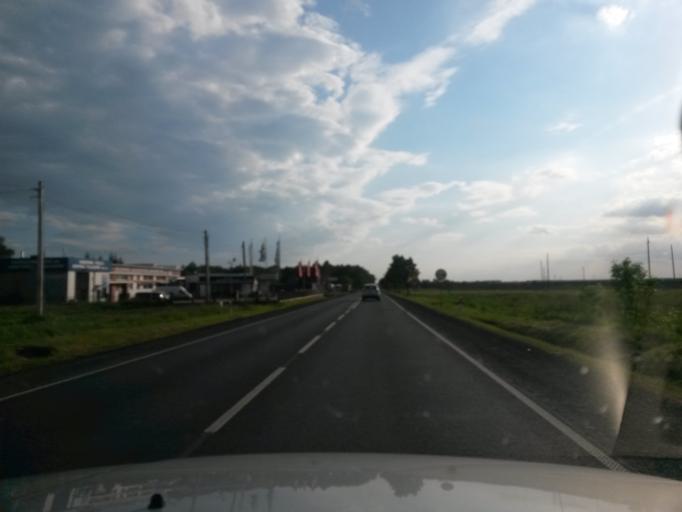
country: PL
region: Lodz Voivodeship
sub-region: Powiat belchatowski
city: Belchatow
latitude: 51.3931
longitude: 19.4089
